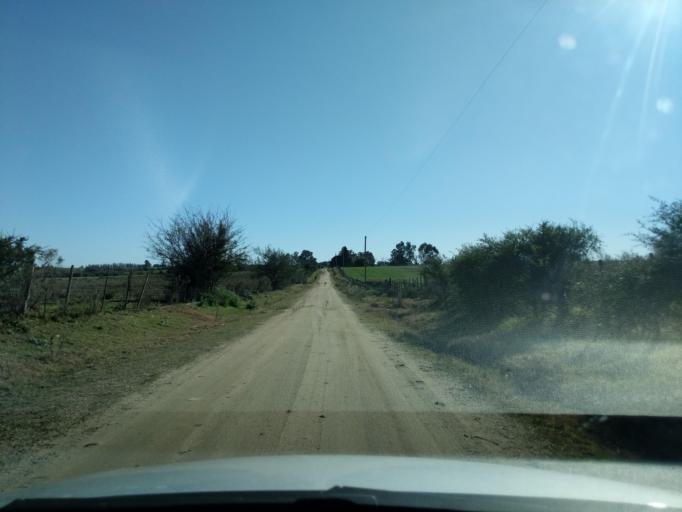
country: UY
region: Florida
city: Florida
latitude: -34.0739
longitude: -56.2677
